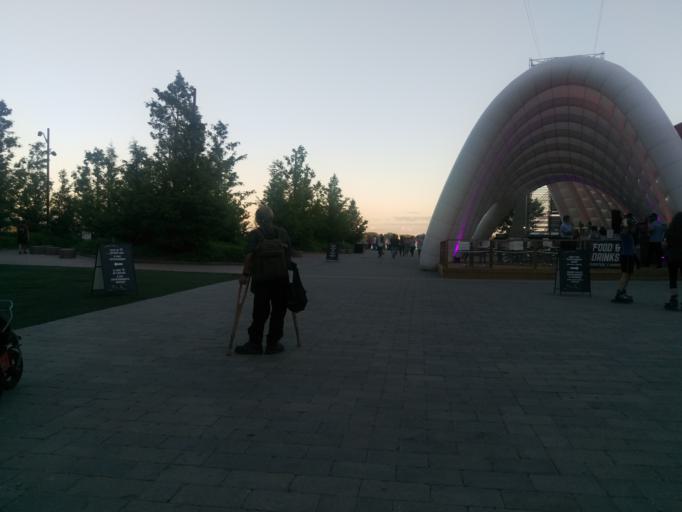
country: CA
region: Ontario
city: Toronto
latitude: 43.6386
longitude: -79.3817
